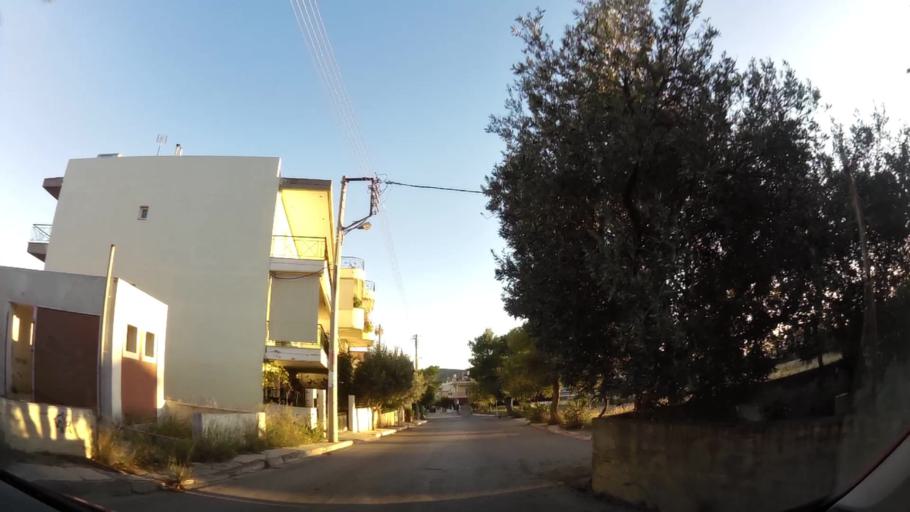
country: GR
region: Attica
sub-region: Nomarchia Dytikis Attikis
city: Ano Liosia
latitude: 38.0866
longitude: 23.6900
